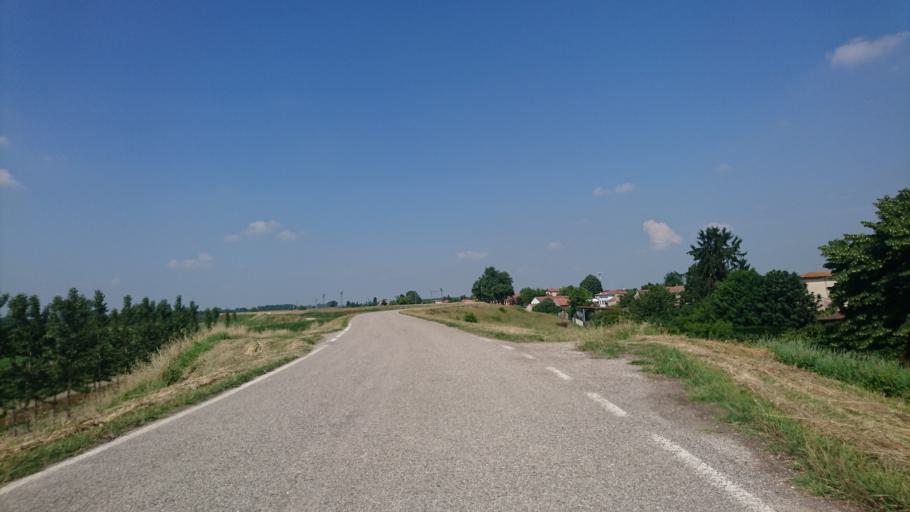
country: IT
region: Lombardy
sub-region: Provincia di Mantova
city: Sustinente
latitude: 45.0680
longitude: 11.0210
